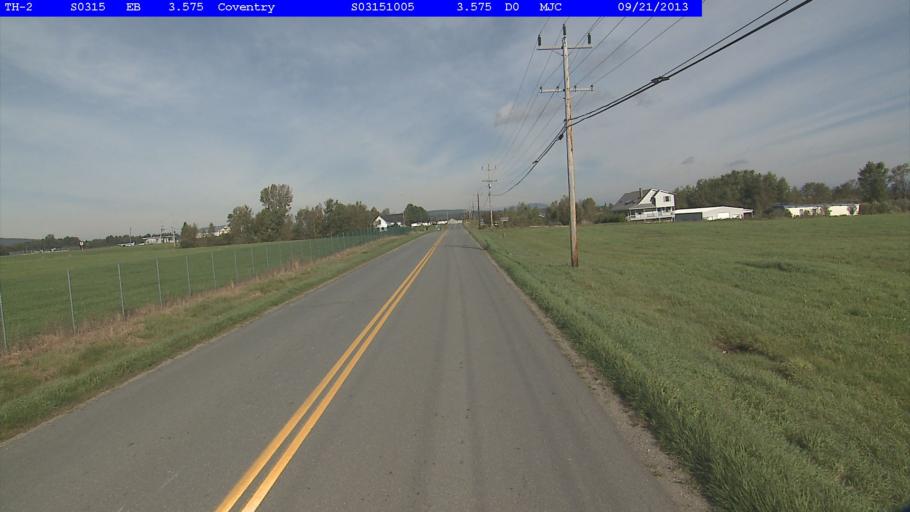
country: US
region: Vermont
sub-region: Orleans County
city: Newport
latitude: 44.8870
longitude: -72.2213
